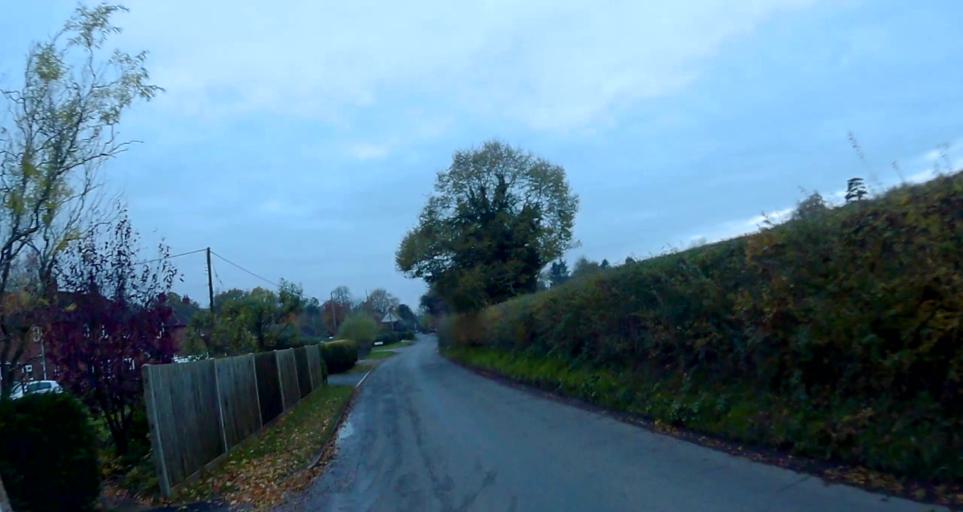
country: GB
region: England
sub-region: Hampshire
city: Old Basing
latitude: 51.2307
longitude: -0.9969
